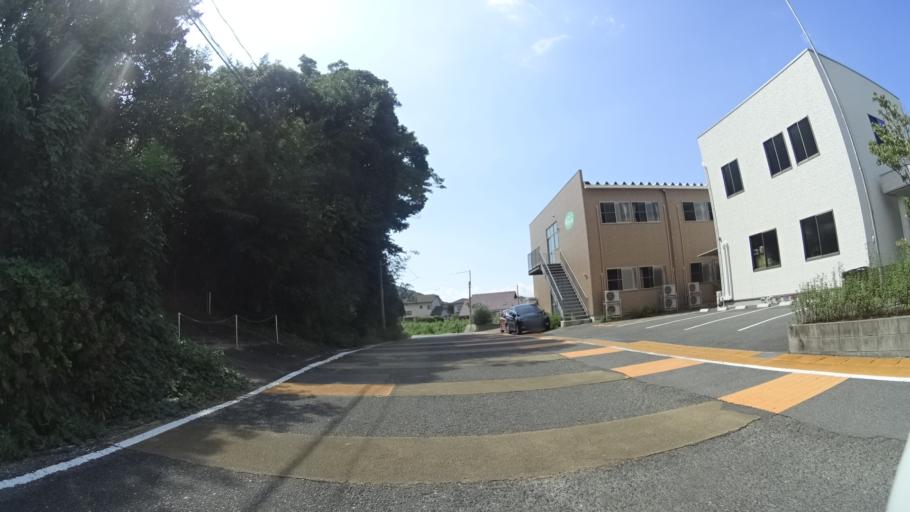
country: JP
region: Yamaguchi
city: Shimonoseki
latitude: 34.0916
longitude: 130.8825
